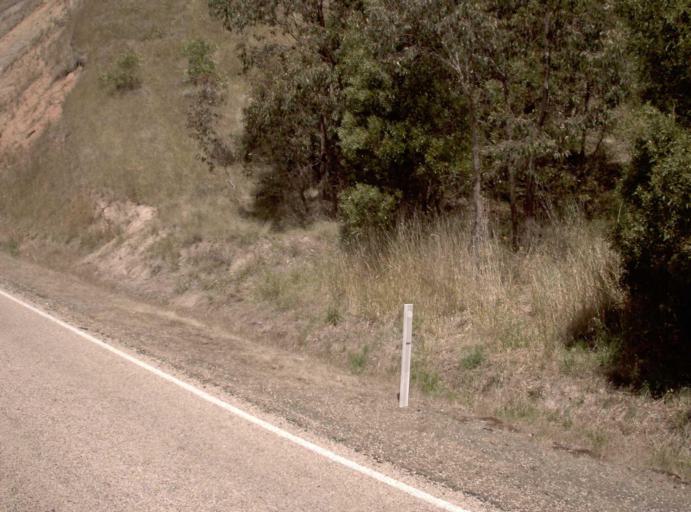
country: AU
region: Victoria
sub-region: Alpine
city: Mount Beauty
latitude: -37.1633
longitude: 147.6579
